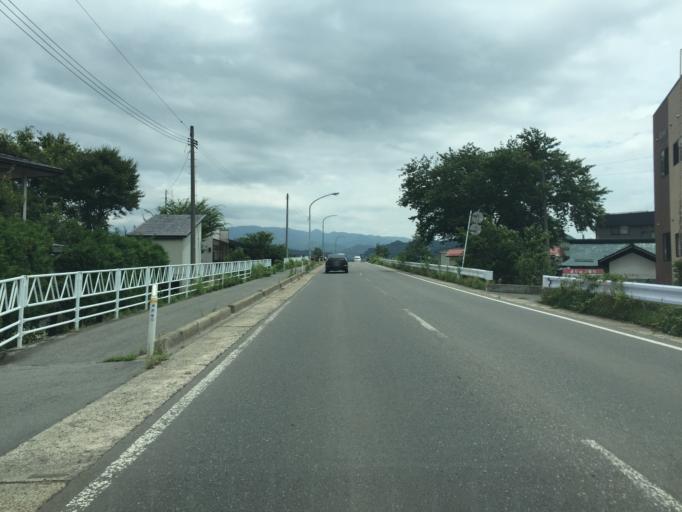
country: JP
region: Yamagata
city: Yonezawa
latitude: 37.9053
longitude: 140.1283
